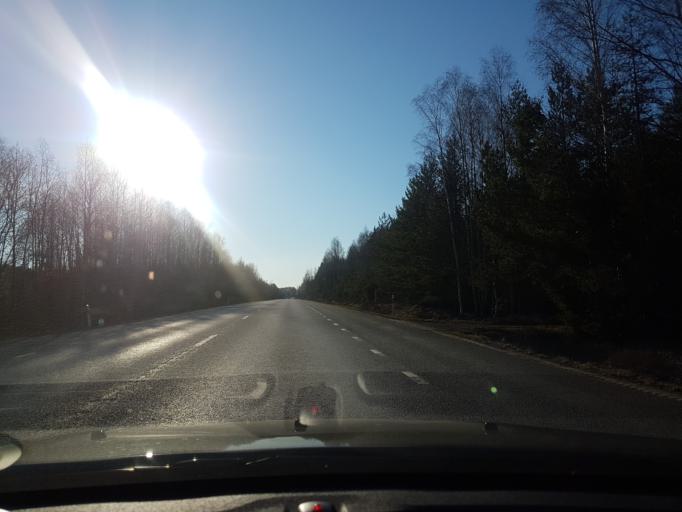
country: SE
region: Uppsala
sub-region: Heby Kommun
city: Morgongava
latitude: 59.8950
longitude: 17.1302
